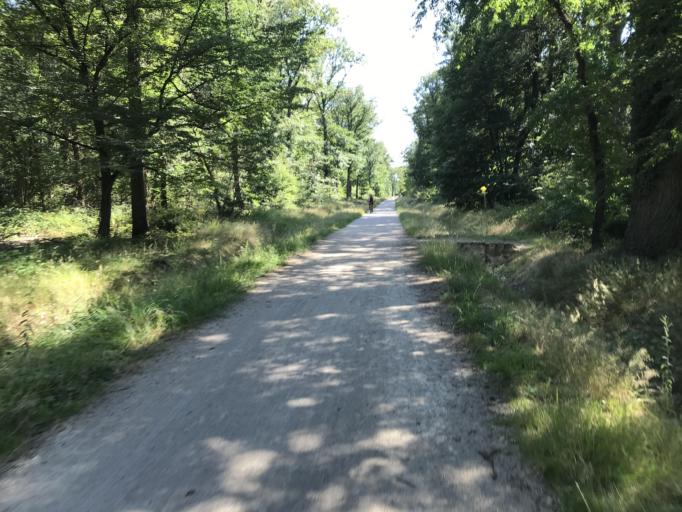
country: FR
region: Ile-de-France
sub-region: Departement de l'Essonne
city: Fleury-Merogis
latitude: 48.6334
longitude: 2.3852
